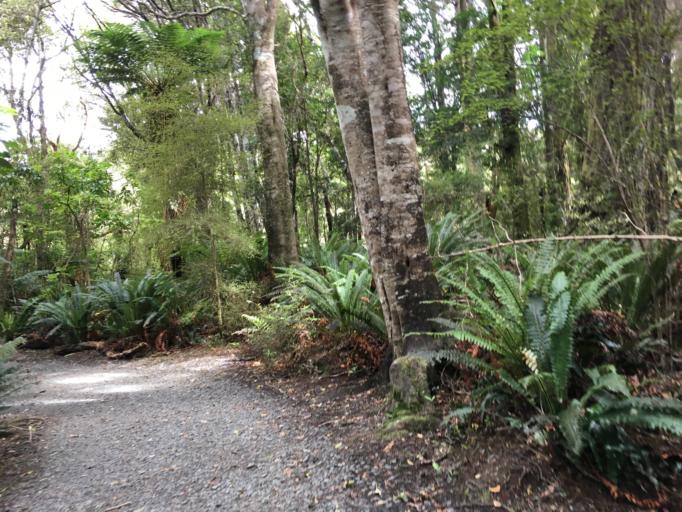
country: NZ
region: Otago
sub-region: Clutha District
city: Papatowai
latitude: -46.5793
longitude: 169.4385
